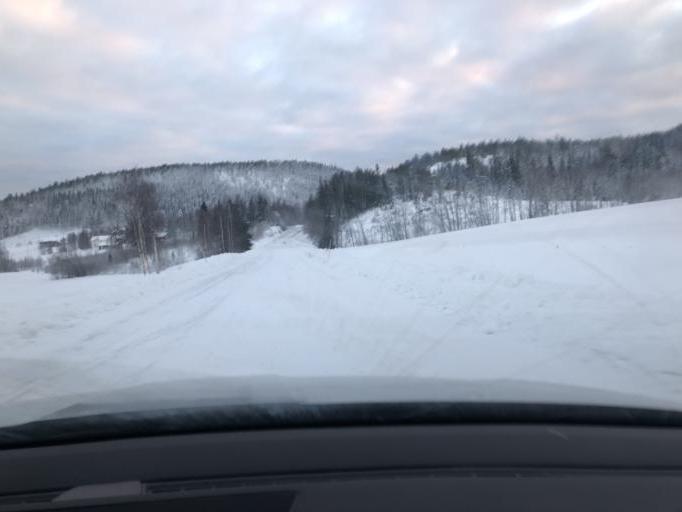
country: SE
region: Vaesternorrland
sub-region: Kramfors Kommun
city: Nordingra
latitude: 62.9879
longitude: 18.2569
